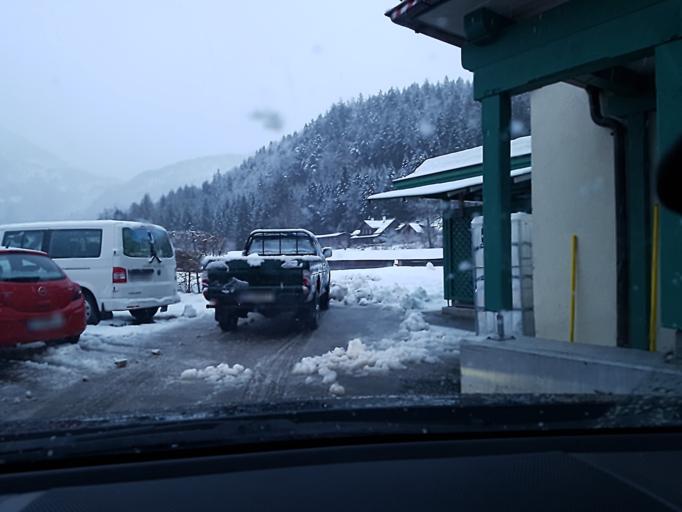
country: AT
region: Styria
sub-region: Politischer Bezirk Liezen
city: Altaussee
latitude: 47.6362
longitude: 13.7683
